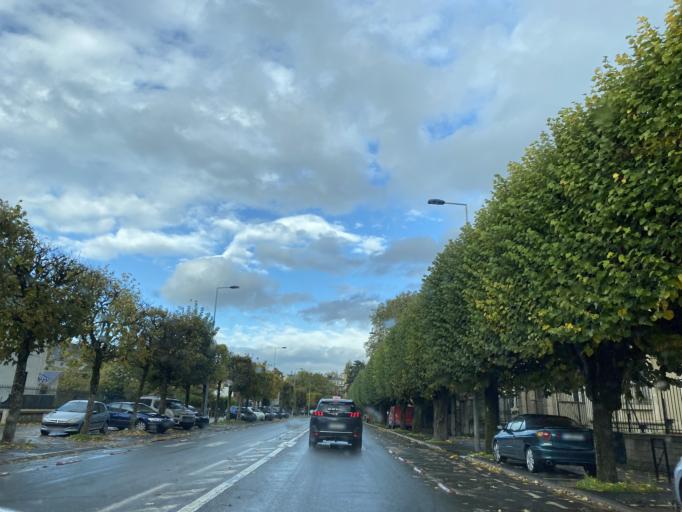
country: FR
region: Centre
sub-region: Departement du Cher
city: Bourges
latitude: 47.0896
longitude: 2.3917
